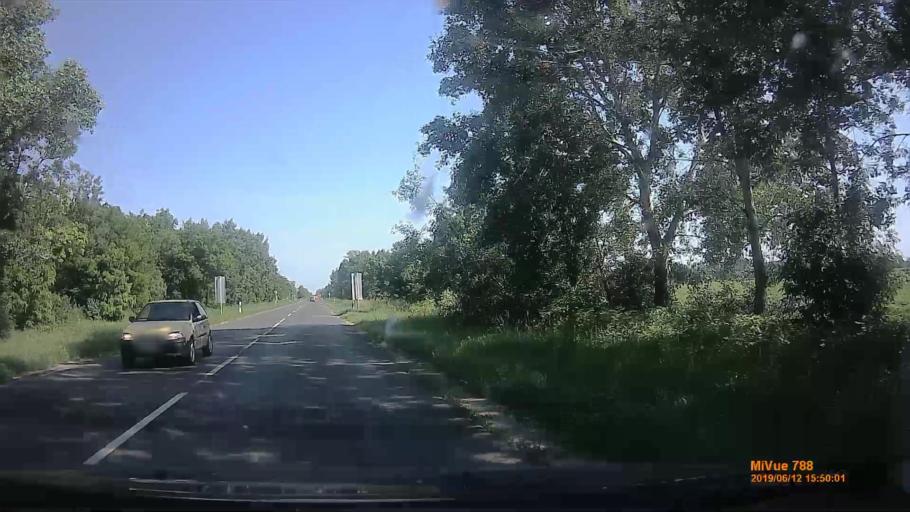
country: HU
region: Csongrad
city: Apatfalva
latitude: 46.1903
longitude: 20.5624
